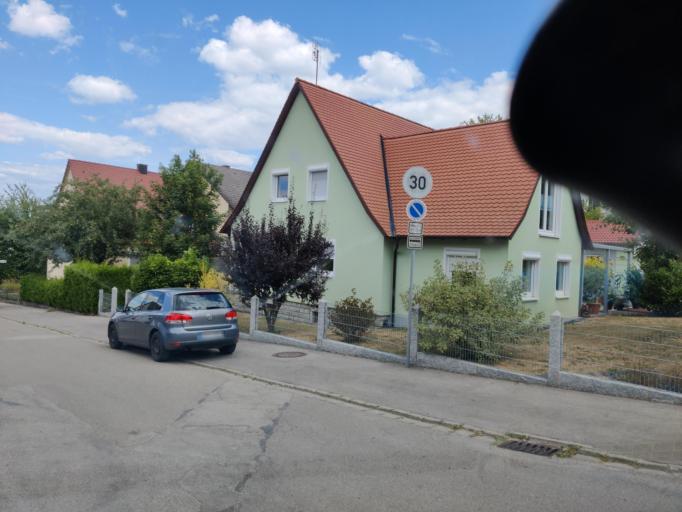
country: DE
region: Bavaria
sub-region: Regierungsbezirk Mittelfranken
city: Thalmassing
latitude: 49.0816
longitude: 11.2142
